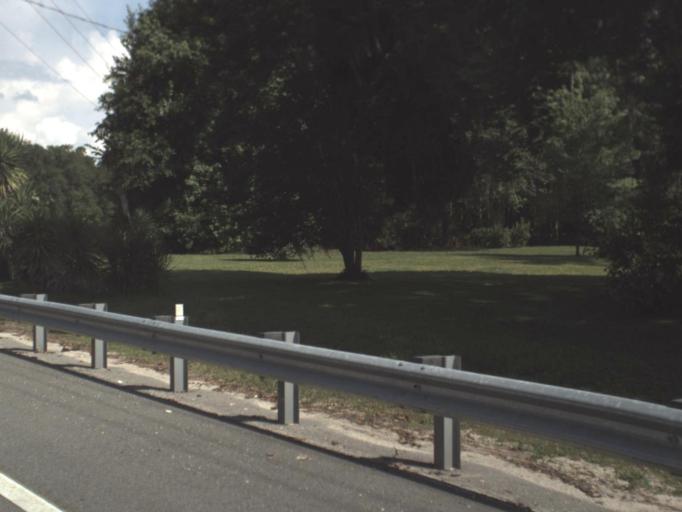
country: US
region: Florida
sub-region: Putnam County
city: Palatka
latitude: 29.6759
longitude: -81.7154
